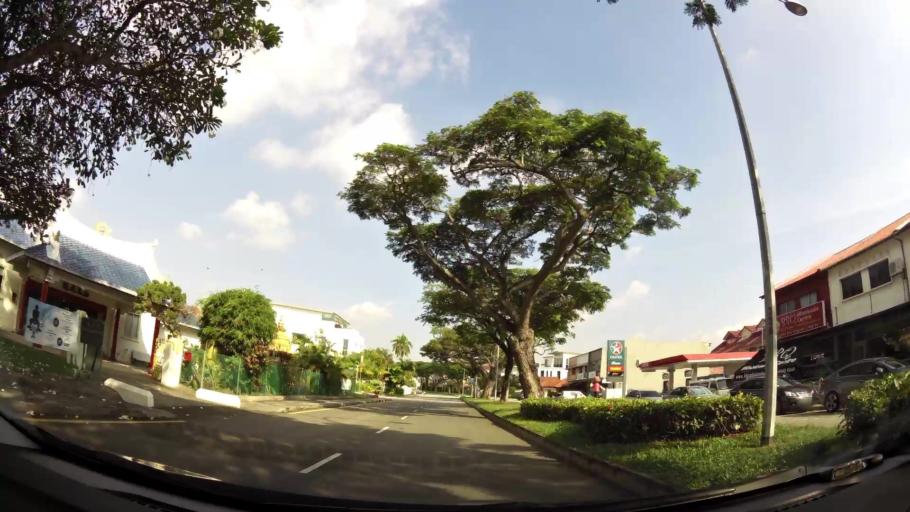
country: SG
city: Singapore
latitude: 1.3150
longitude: 103.9189
